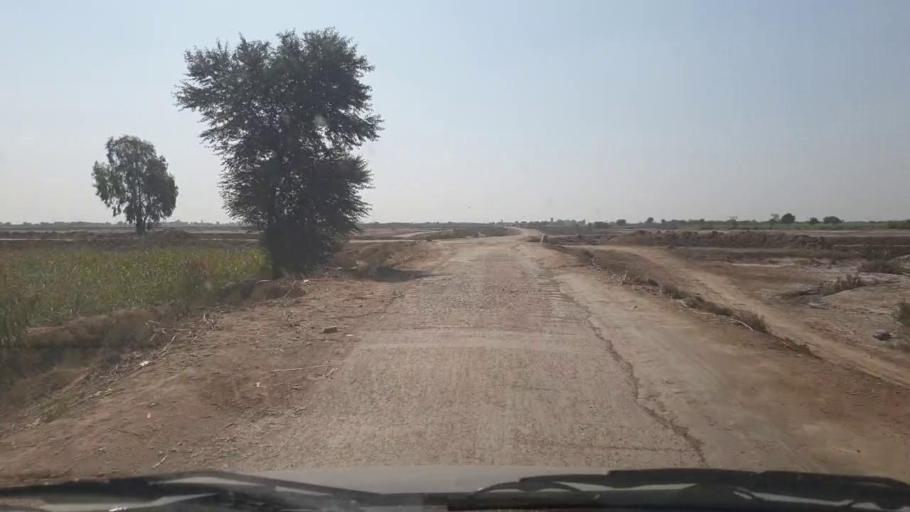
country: PK
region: Sindh
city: Samaro
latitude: 25.2421
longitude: 69.3423
